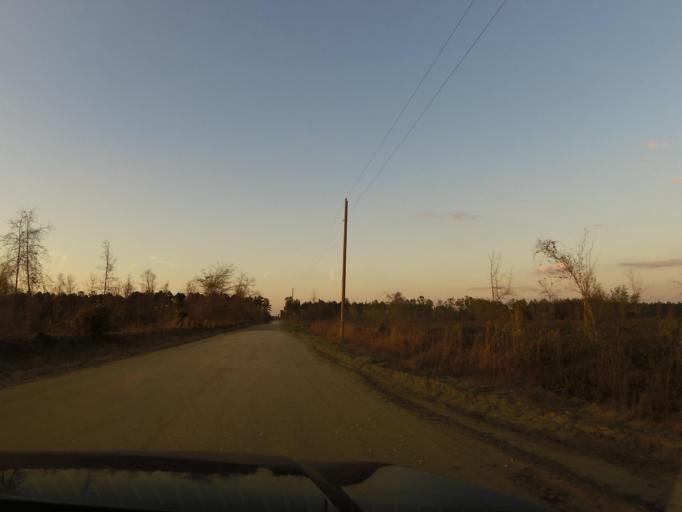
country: US
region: Florida
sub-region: Clay County
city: Green Cove Springs
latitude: 29.9028
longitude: -81.7802
